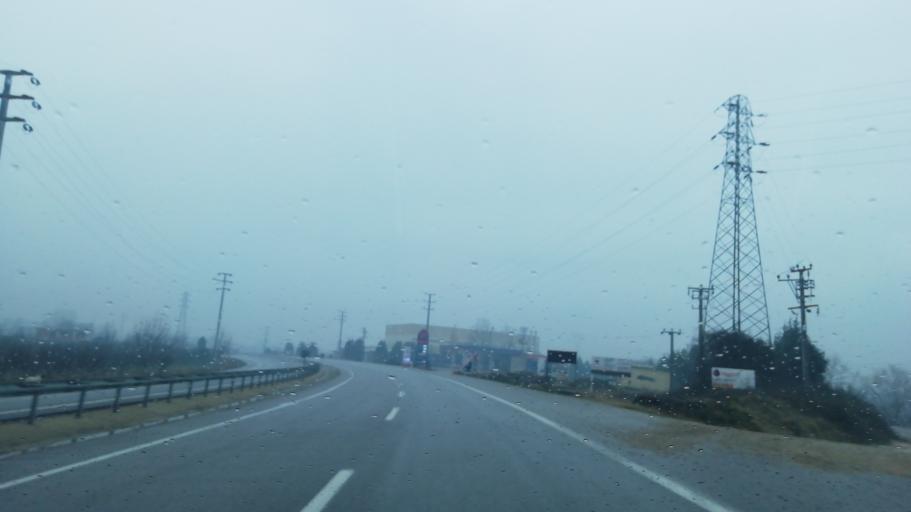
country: TR
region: Sakarya
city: Akyazi
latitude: 40.6417
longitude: 30.6137
